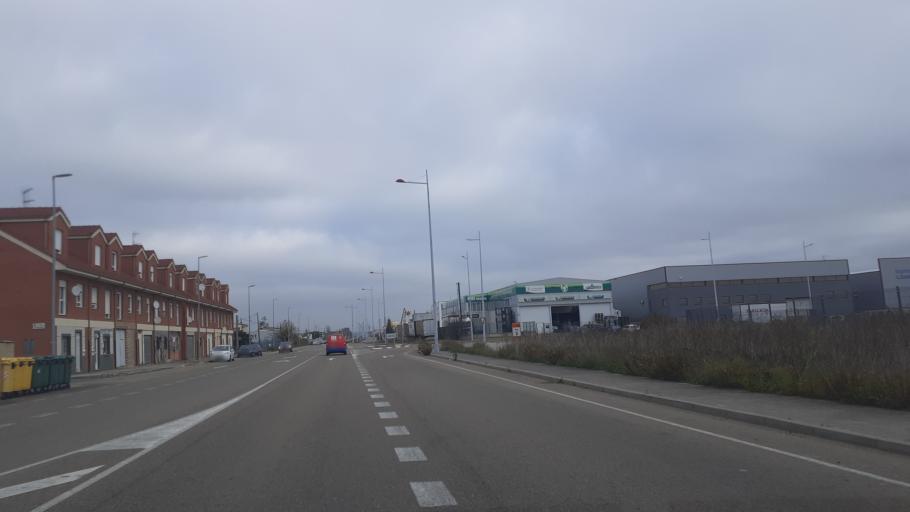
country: ES
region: Castille and Leon
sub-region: Provincia de Leon
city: Onzonilla
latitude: 42.5395
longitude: -5.5900
